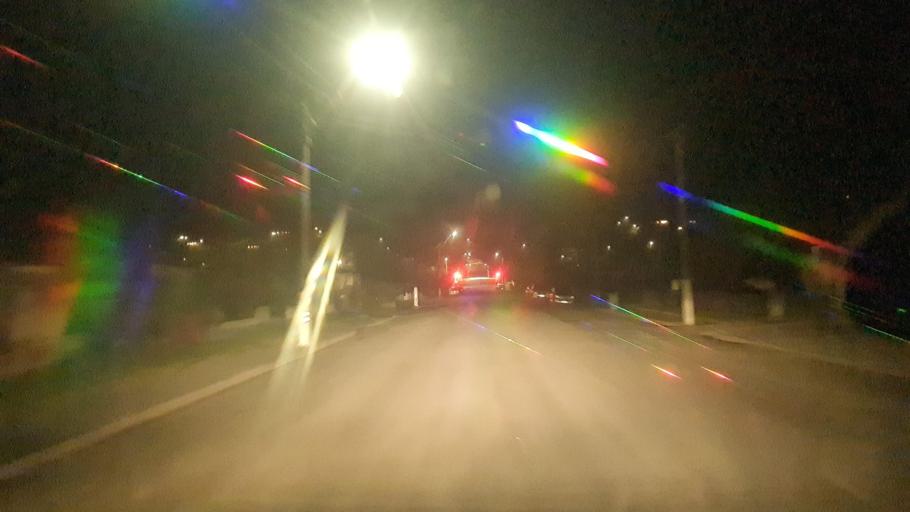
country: NZ
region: Otago
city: Oamaru
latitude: -45.0891
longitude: 170.9785
